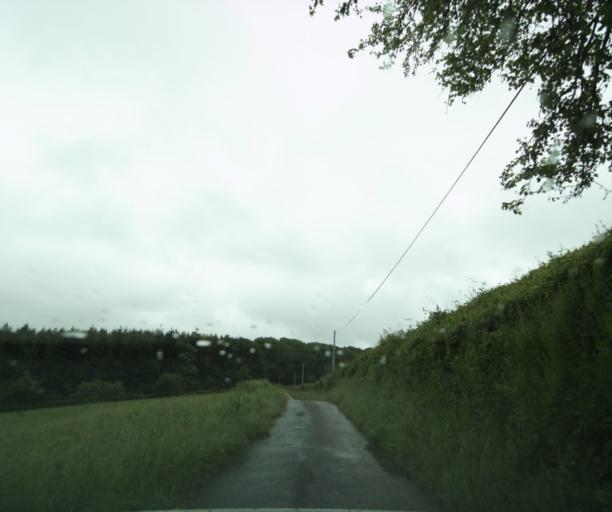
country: FR
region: Bourgogne
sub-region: Departement de Saone-et-Loire
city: Charolles
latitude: 46.4938
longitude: 4.4047
